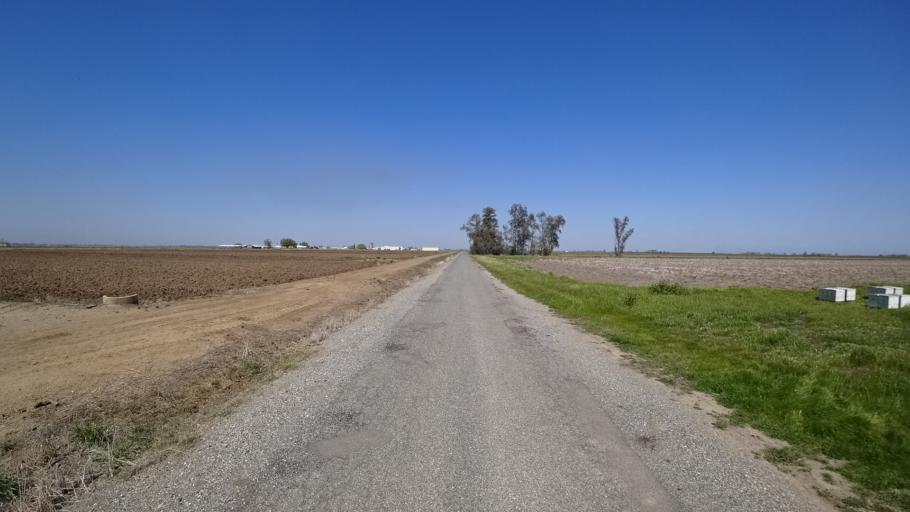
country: US
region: California
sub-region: Glenn County
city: Willows
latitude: 39.4881
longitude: -122.1263
